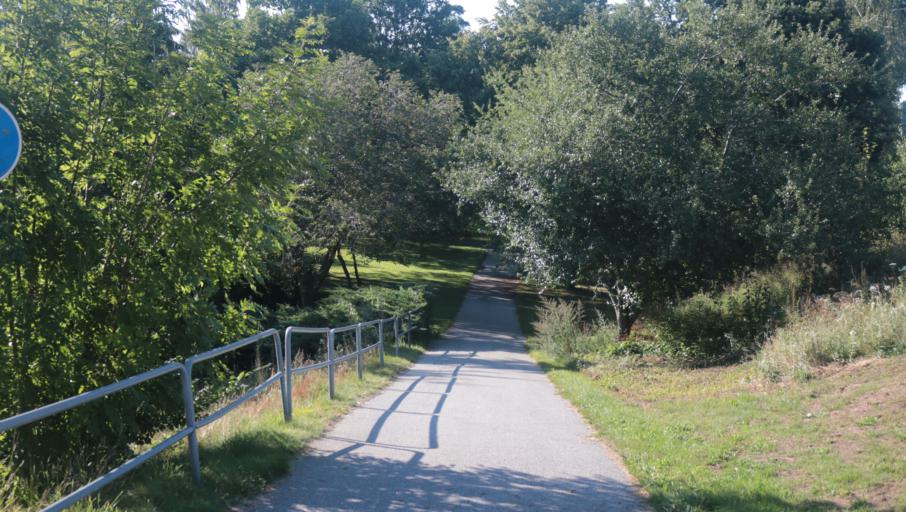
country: SE
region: Blekinge
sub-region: Karlshamns Kommun
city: Svangsta
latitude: 56.2628
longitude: 14.7706
